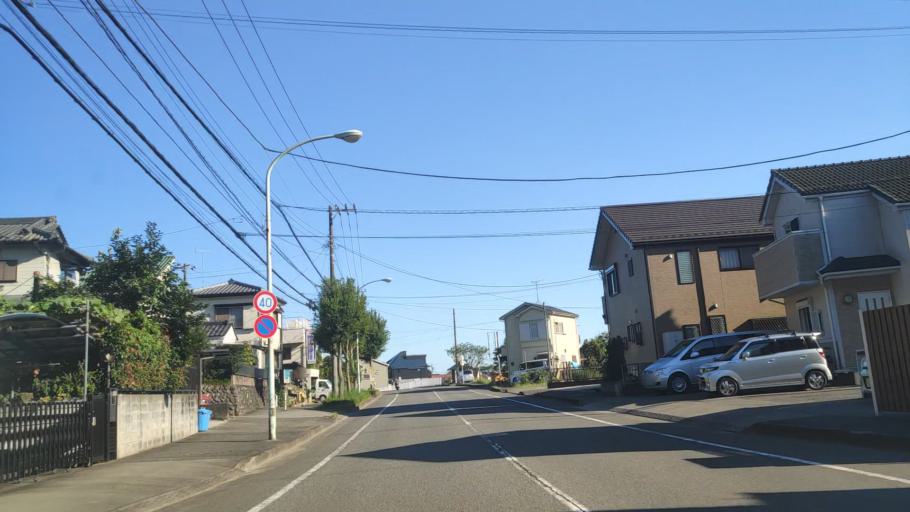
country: JP
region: Tokyo
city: Hachioji
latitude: 35.6082
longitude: 139.3143
